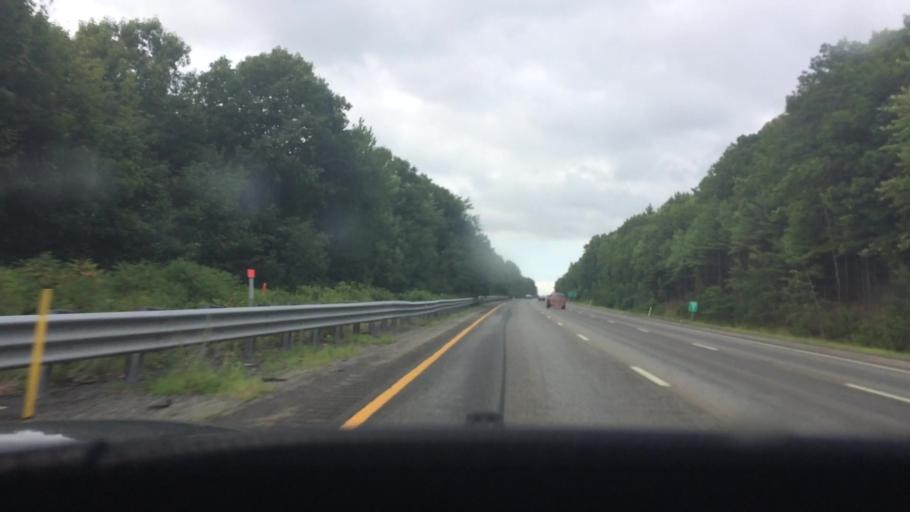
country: US
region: Massachusetts
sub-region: Worcester County
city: Harvard
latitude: 42.4956
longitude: -71.5372
